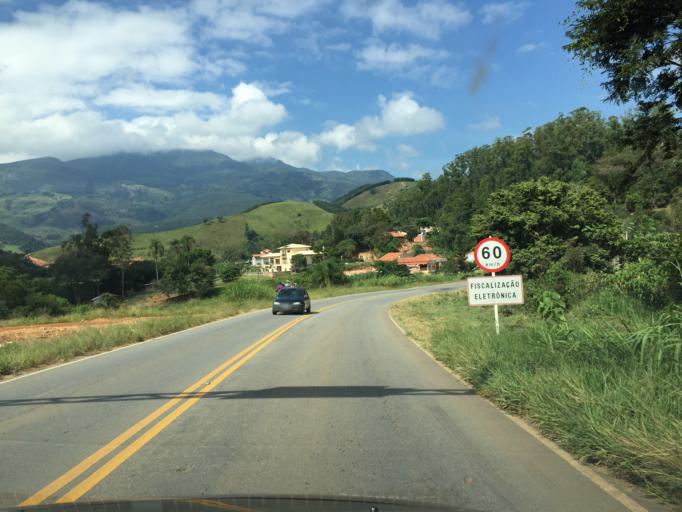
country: BR
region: Minas Gerais
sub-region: Passa Quatro
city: Passa Quatro
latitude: -22.3730
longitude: -44.9620
